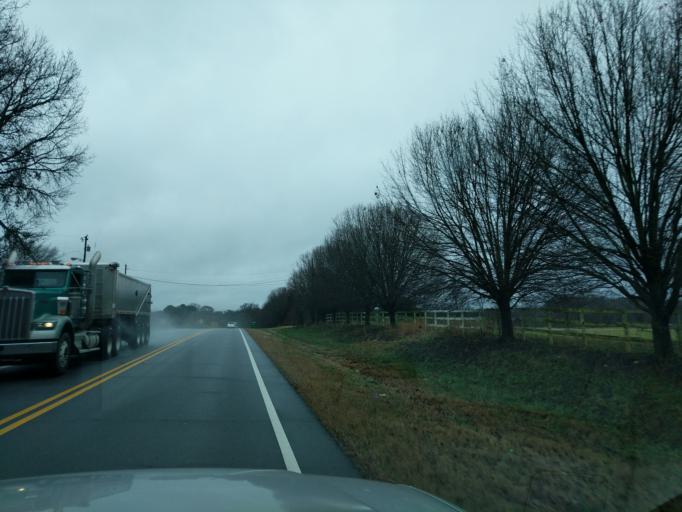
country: US
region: Georgia
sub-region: Franklin County
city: Lavonia
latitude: 34.3846
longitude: -83.0944
